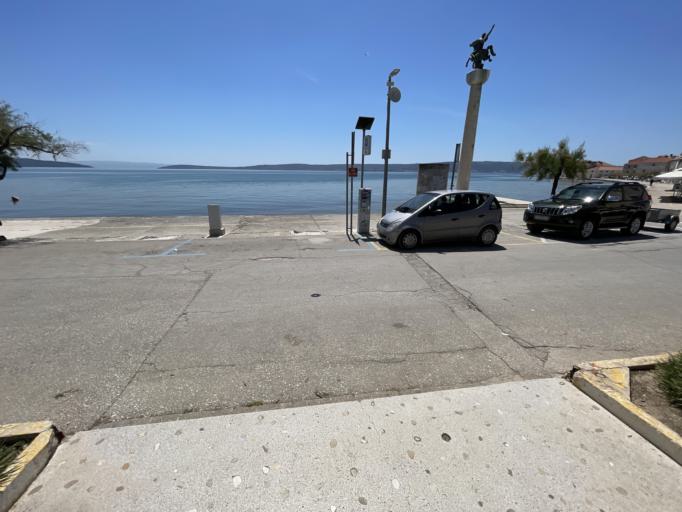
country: HR
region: Splitsko-Dalmatinska
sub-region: Grad Trogir
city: Trogir
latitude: 43.5496
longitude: 16.3417
